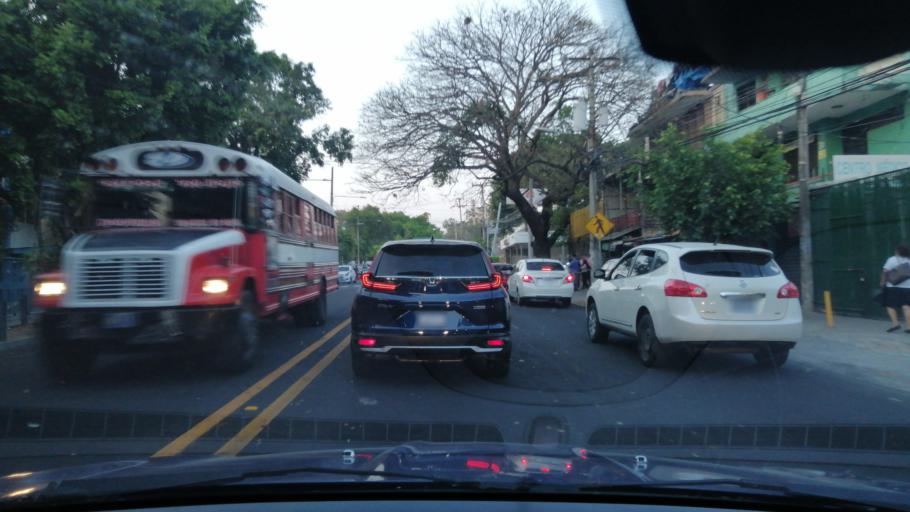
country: SV
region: San Salvador
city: Mejicanos
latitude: 13.7138
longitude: -89.2034
